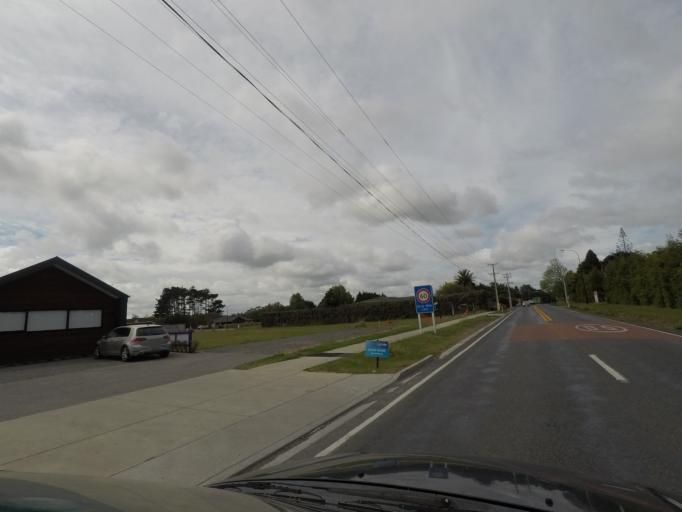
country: NZ
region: Auckland
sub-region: Auckland
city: Rosebank
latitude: -36.7674
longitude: 174.5873
